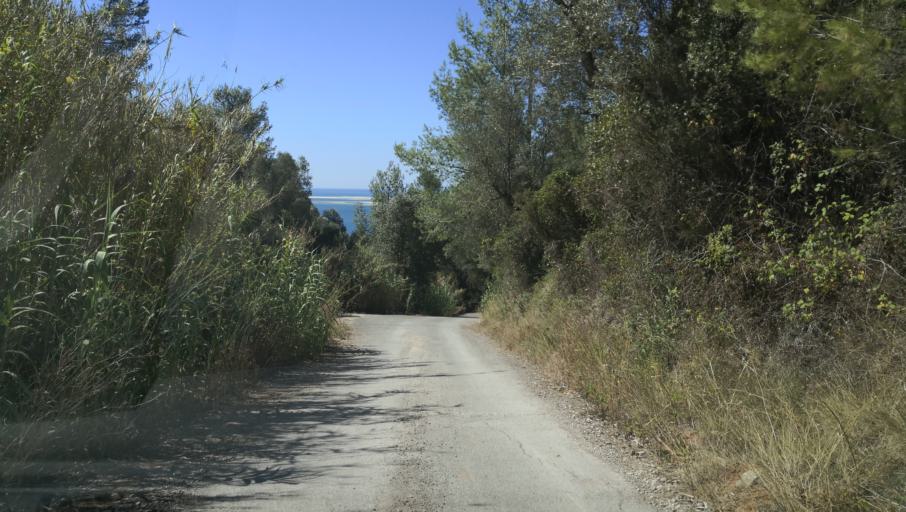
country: PT
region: Setubal
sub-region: Setubal
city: Setubal
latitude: 38.5141
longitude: -8.9145
